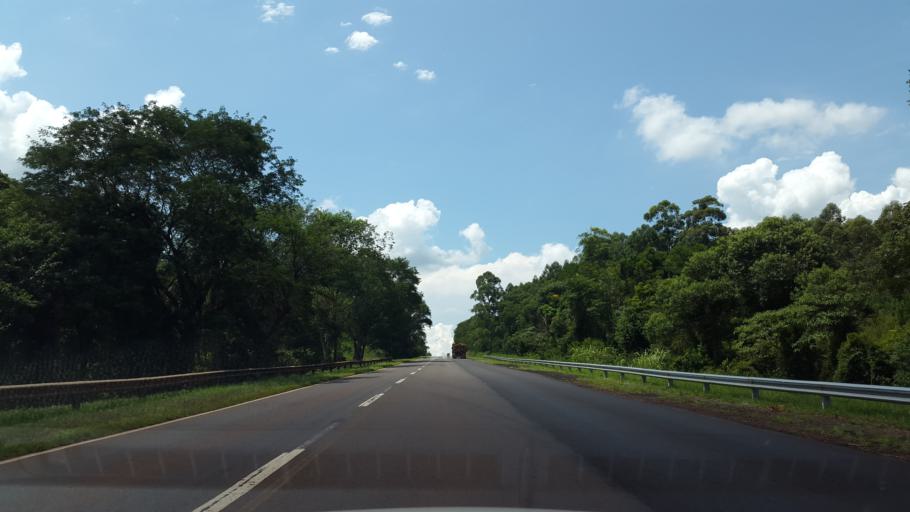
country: AR
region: Misiones
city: El Alcazar
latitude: -26.7298
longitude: -54.8711
